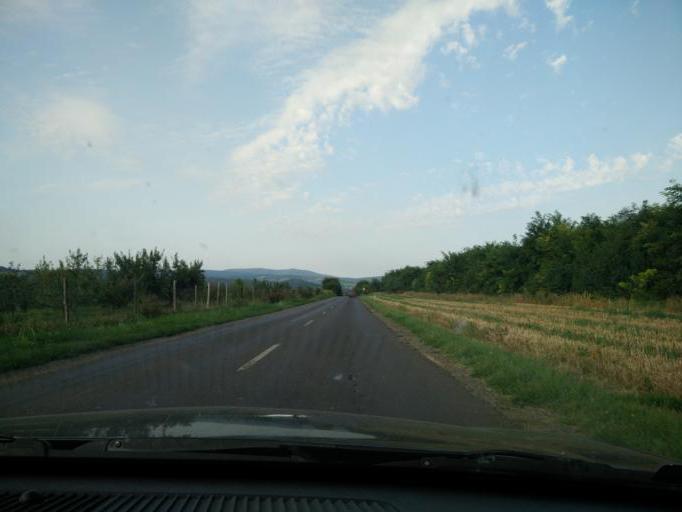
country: HU
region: Tolna
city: Nagymanyok
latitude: 46.2902
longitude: 18.4813
